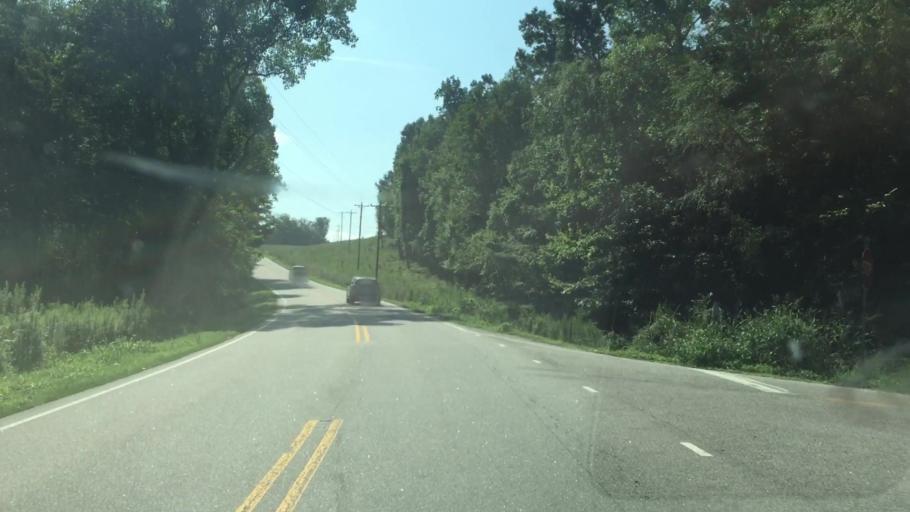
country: US
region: North Carolina
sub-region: Anson County
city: Burnsville
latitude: 35.1088
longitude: -80.3356
